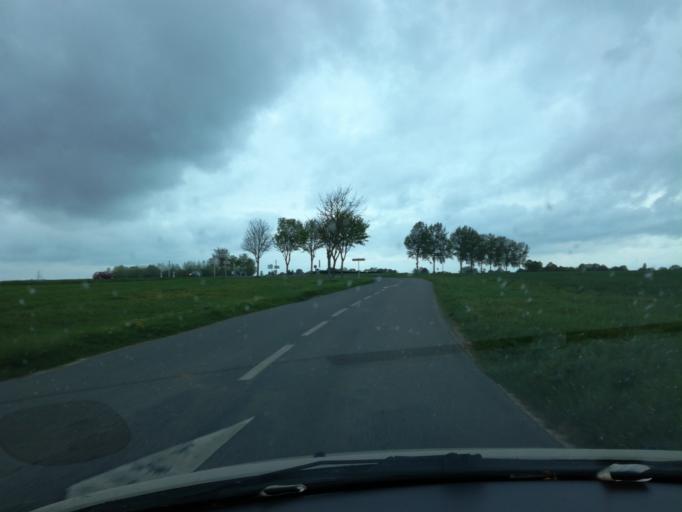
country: FR
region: Picardie
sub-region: Departement de la Somme
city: Poix-de-Picardie
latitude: 49.8212
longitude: 1.9576
